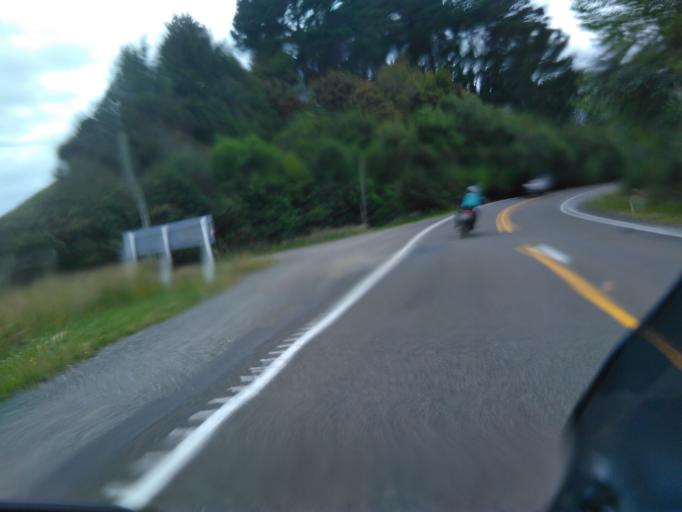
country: NZ
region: Bay of Plenty
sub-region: Opotiki District
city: Opotiki
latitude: -38.3940
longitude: 177.5612
